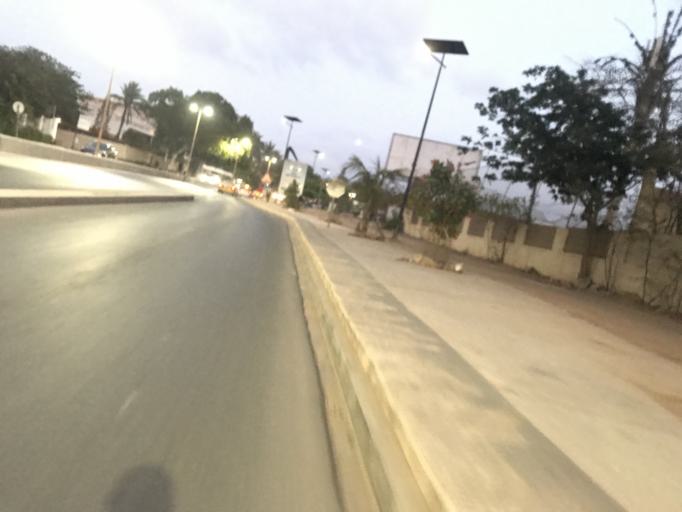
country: SN
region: Dakar
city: Mermoz Boabab
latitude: 14.7005
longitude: -17.4742
